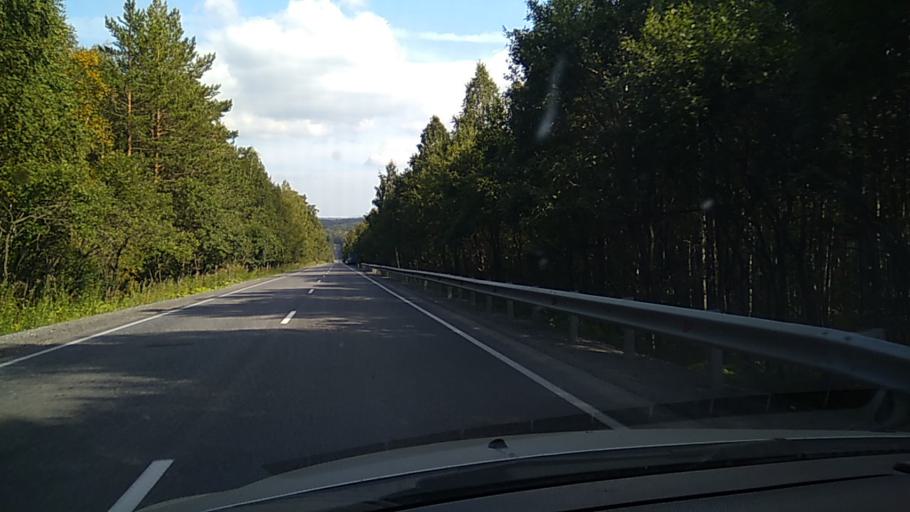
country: RU
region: Chelyabinsk
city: Syrostan
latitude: 55.1200
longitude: 59.8258
